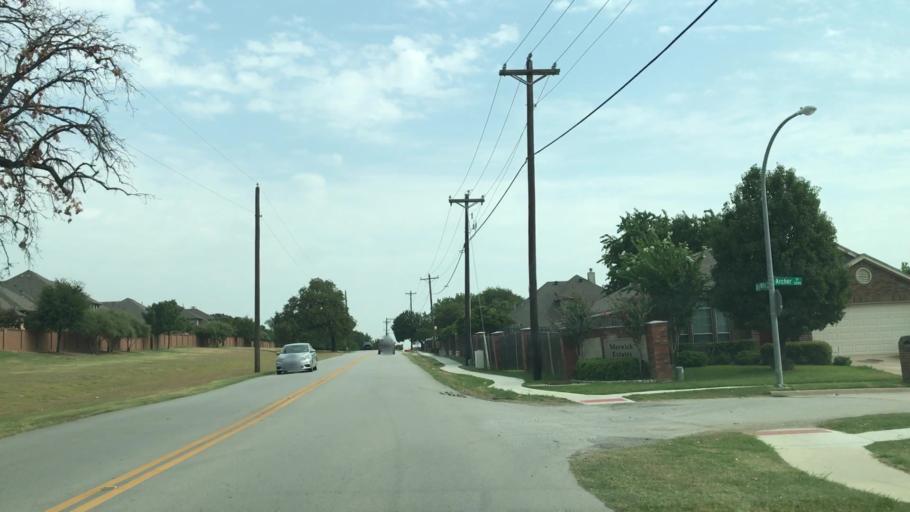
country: US
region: Texas
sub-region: Tarrant County
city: Keller
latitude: 32.9145
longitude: -97.2725
